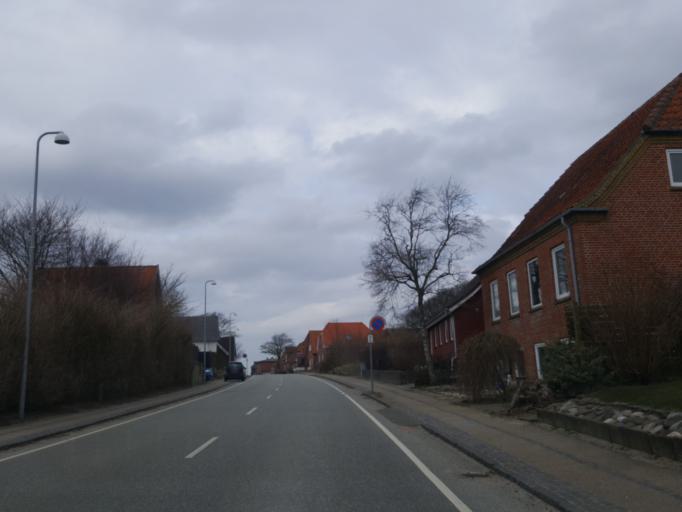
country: DK
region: Central Jutland
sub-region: Lemvig Kommune
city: Lemvig
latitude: 56.4331
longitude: 8.2078
